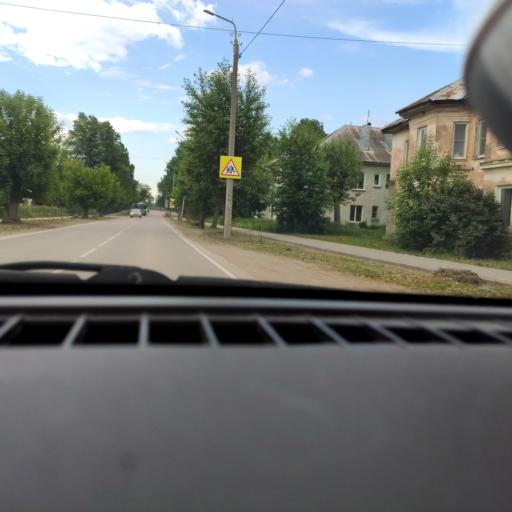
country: RU
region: Perm
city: Krasnokamsk
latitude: 58.0700
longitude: 55.7990
